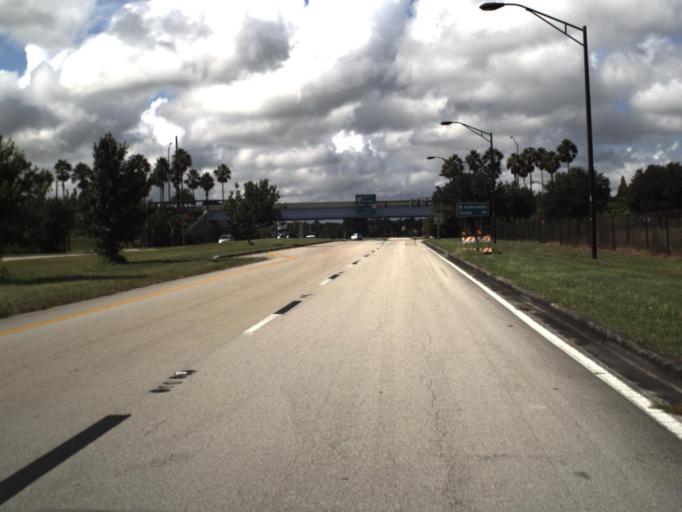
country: US
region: Florida
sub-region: Polk County
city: Winston
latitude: 28.0100
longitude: -82.0152
